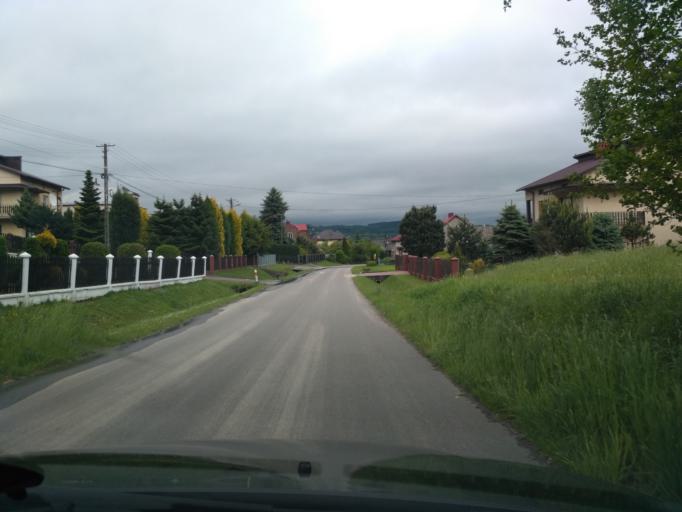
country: PL
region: Subcarpathian Voivodeship
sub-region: Powiat jasielski
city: Brzyska
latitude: 49.8234
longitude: 21.3846
